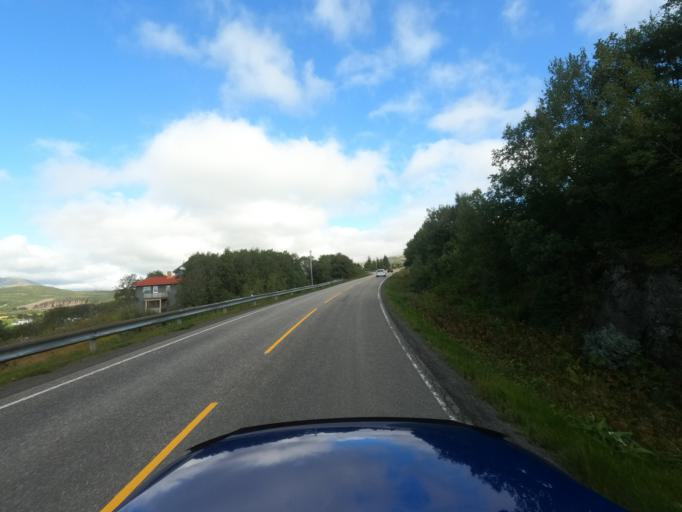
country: NO
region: Nordland
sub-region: Vestvagoy
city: Leknes
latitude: 68.1516
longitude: 13.6729
